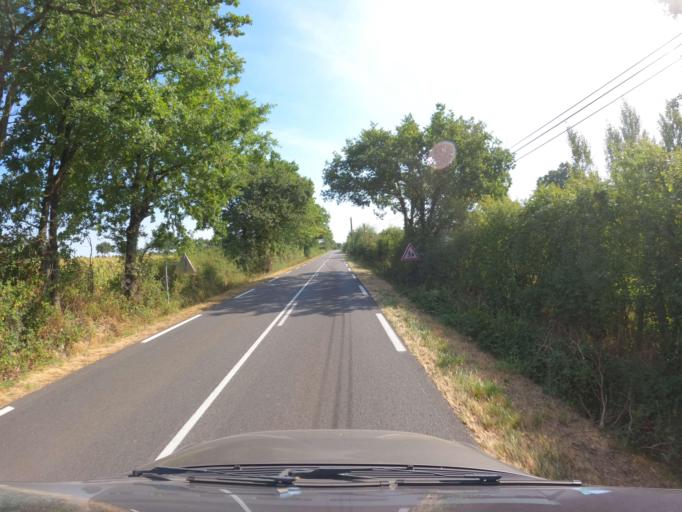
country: FR
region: Pays de la Loire
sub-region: Departement de la Vendee
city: Saint-Christophe-du-Ligneron
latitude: 46.8406
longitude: -1.7489
